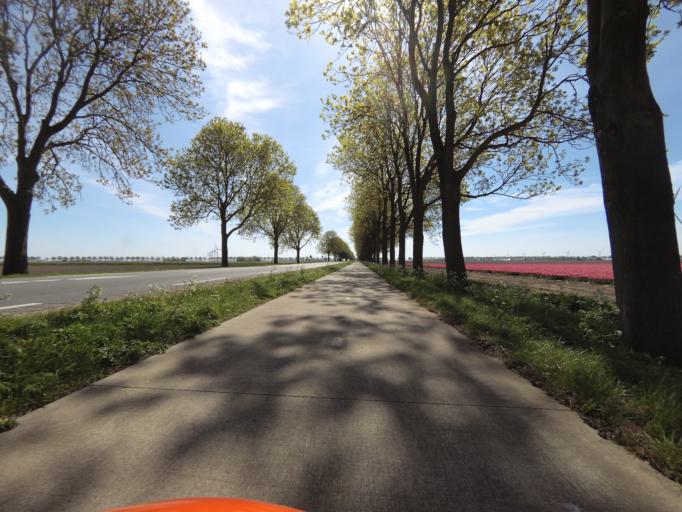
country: NL
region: Flevoland
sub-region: Gemeente Dronten
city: Biddinghuizen
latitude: 52.4913
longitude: 5.6539
